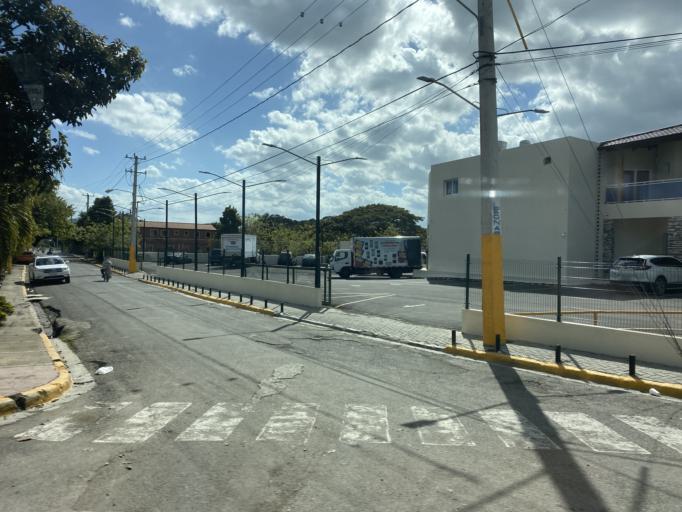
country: DO
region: Espaillat
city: Jamao al Norte
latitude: 19.6693
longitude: -70.3690
